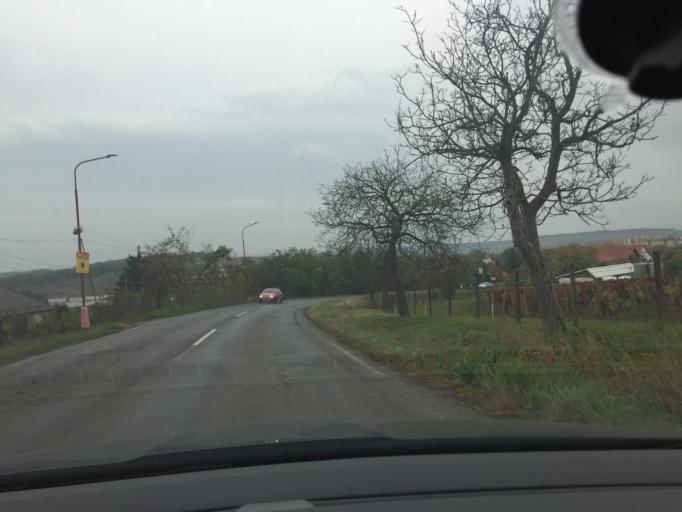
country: SK
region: Banskobystricky
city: Velky Krtis
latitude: 48.2125
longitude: 19.3657
